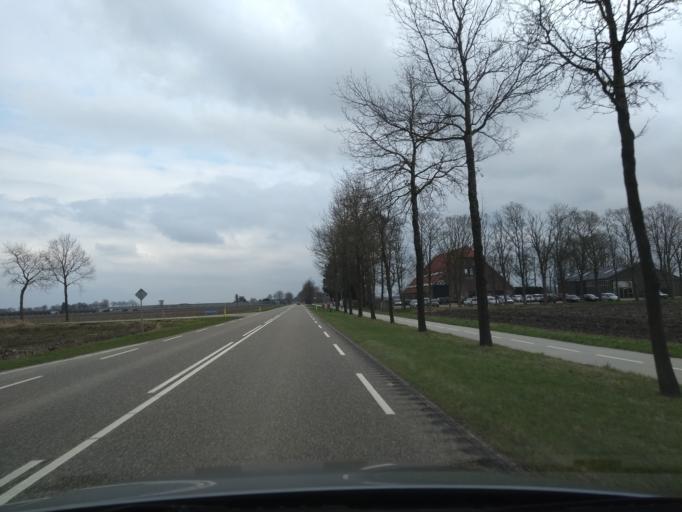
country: NL
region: Overijssel
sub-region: Gemeente Steenwijkerland
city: Vollenhove
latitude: 52.7049
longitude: 5.8899
